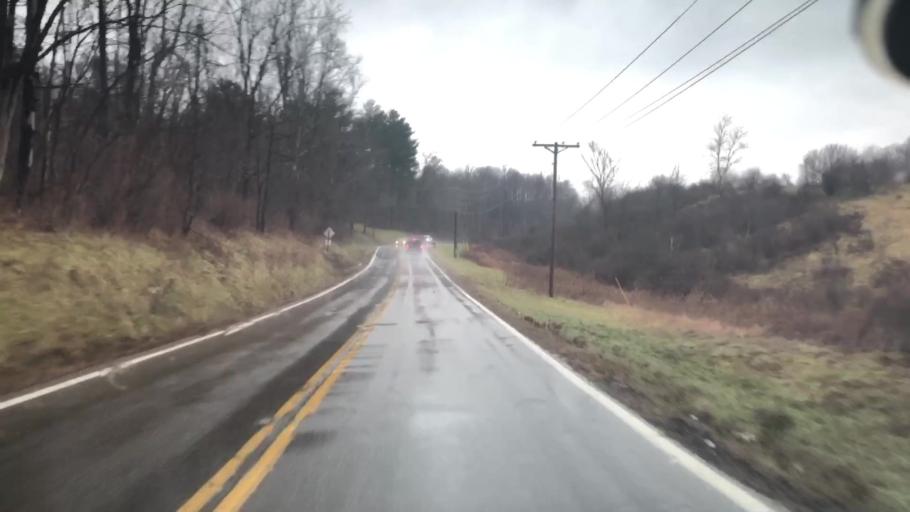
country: US
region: Ohio
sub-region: Harrison County
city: Cadiz
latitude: 40.1669
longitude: -80.9835
